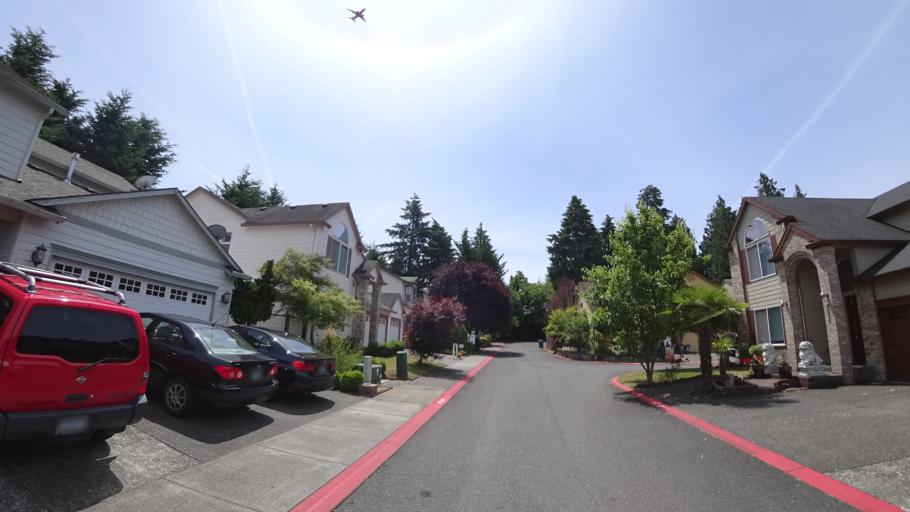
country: US
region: Oregon
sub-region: Multnomah County
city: Fairview
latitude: 45.5468
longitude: -122.4923
